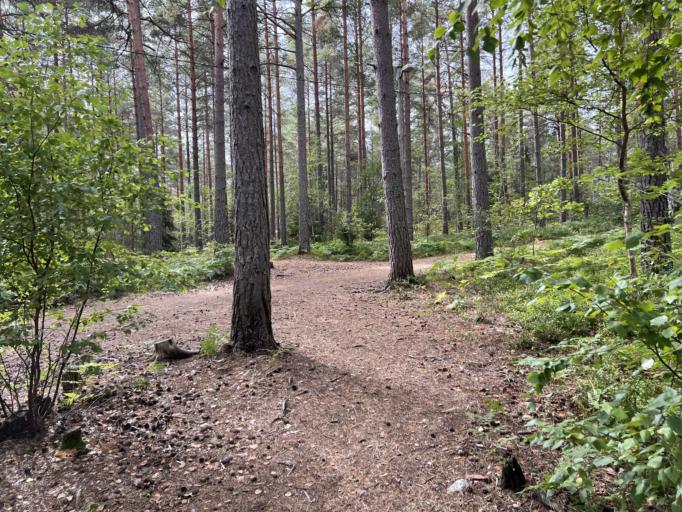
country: SE
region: Stockholm
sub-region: Vallentuna Kommun
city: Vallentuna
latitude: 59.4946
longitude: 18.0796
